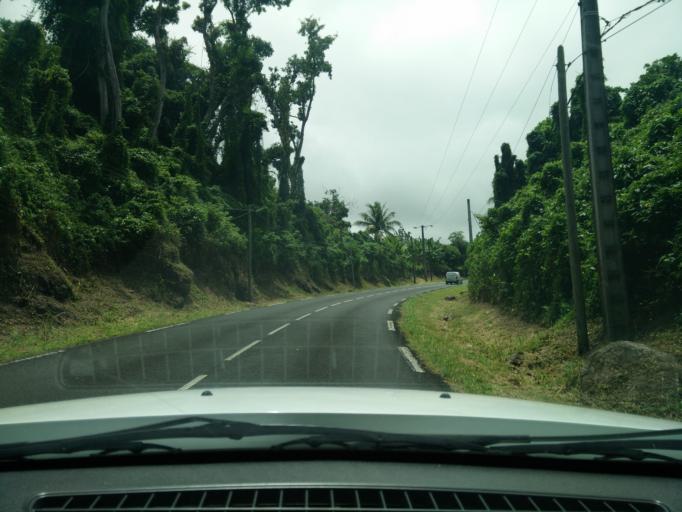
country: GP
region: Guadeloupe
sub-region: Guadeloupe
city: Trois-Rivieres
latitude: 15.9784
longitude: -61.6296
